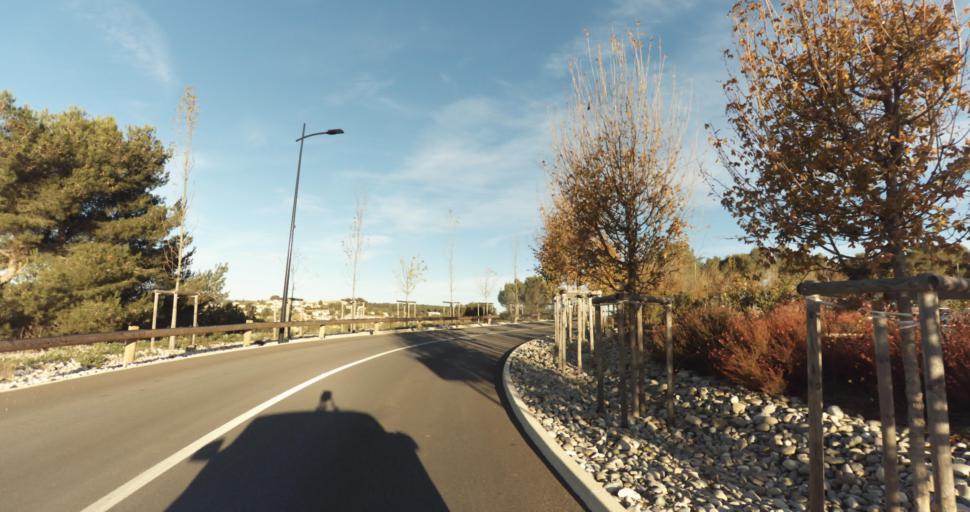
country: FR
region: Provence-Alpes-Cote d'Azur
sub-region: Departement des Bouches-du-Rhone
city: Venelles
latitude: 43.5957
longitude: 5.4919
